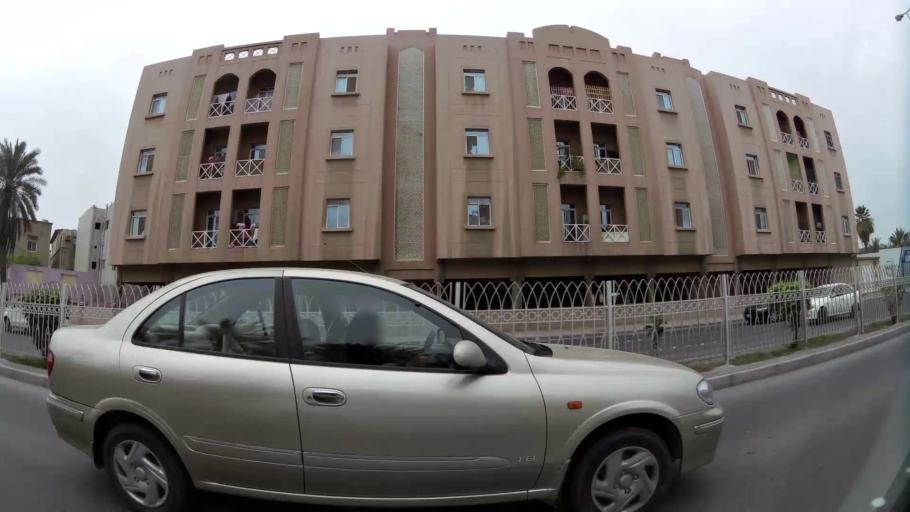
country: BH
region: Manama
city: Jidd Hafs
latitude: 26.2196
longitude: 50.5643
